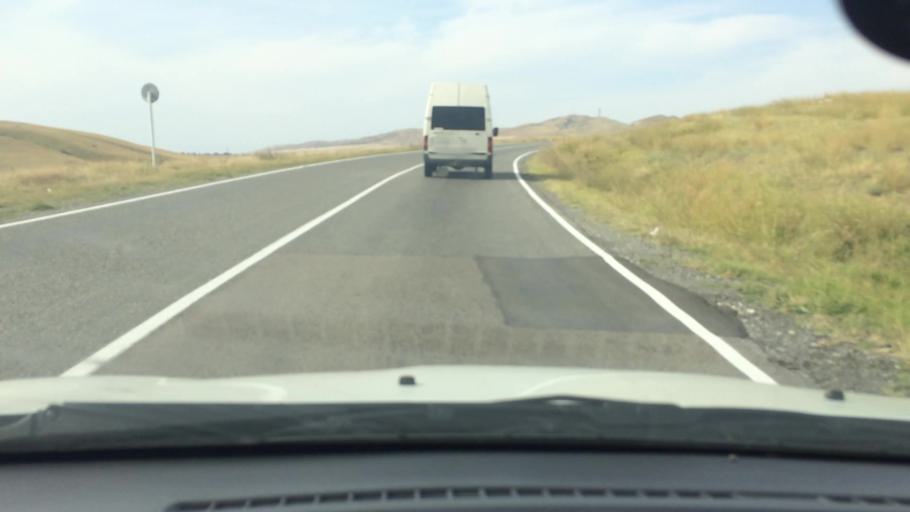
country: GE
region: Kvemo Kartli
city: Rust'avi
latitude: 41.5250
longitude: 44.9815
